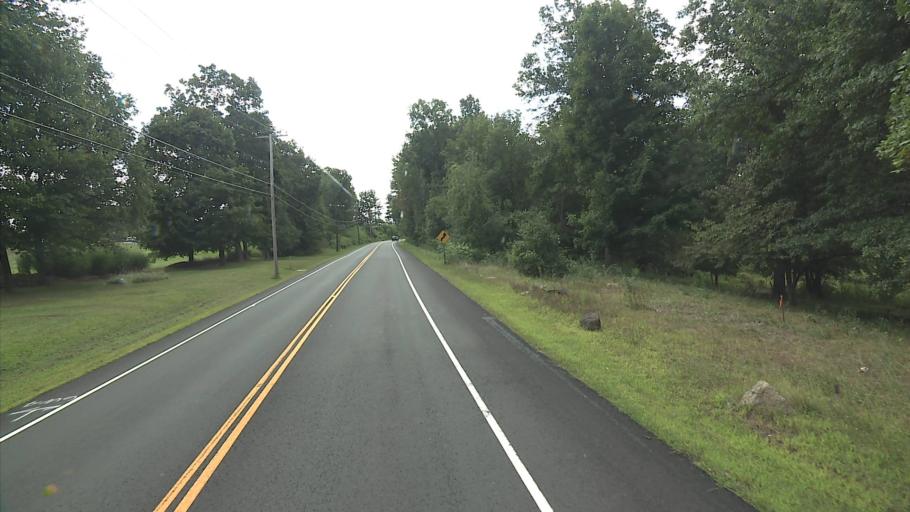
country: US
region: Connecticut
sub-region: Hartford County
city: West Hartford
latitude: 41.8113
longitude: -72.7590
